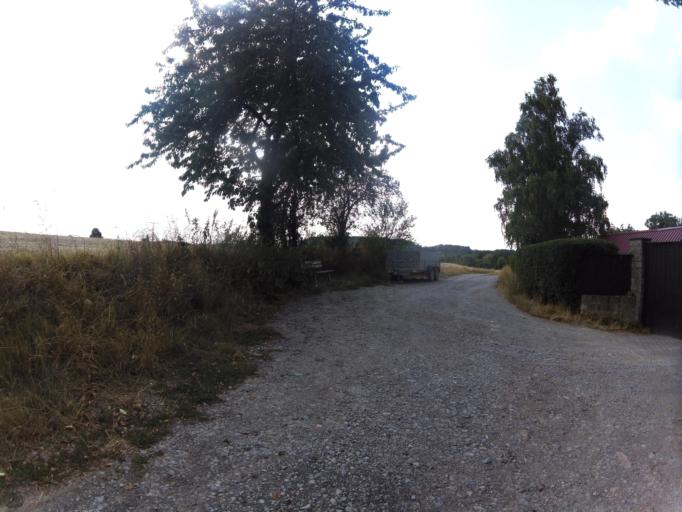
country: DE
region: Bavaria
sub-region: Regierungsbezirk Unterfranken
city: Ochsenfurt
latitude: 49.6593
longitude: 10.0663
